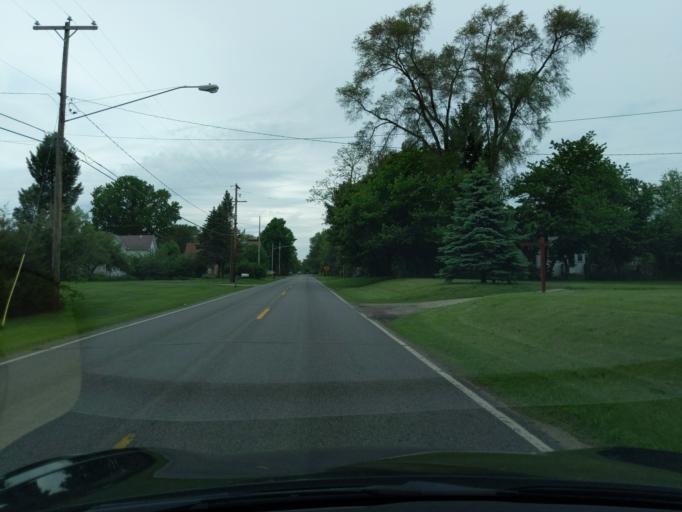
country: US
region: Michigan
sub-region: Ingham County
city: Leslie
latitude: 42.3775
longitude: -84.3492
